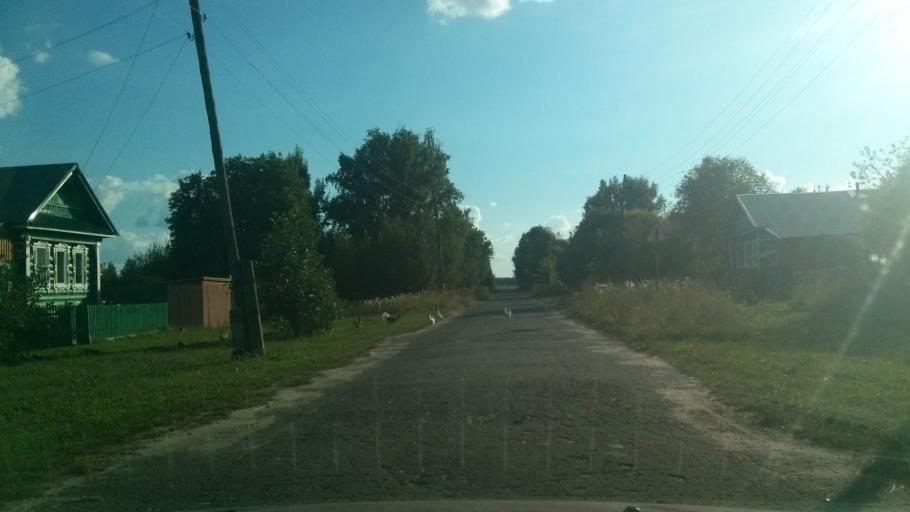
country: RU
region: Nizjnij Novgorod
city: Shimorskoye
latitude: 55.3040
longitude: 41.8402
